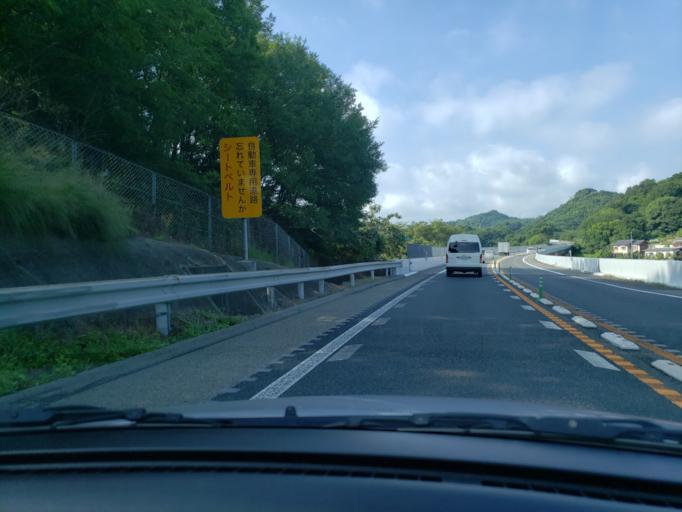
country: JP
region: Hiroshima
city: Onomichi
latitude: 34.3965
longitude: 133.2083
